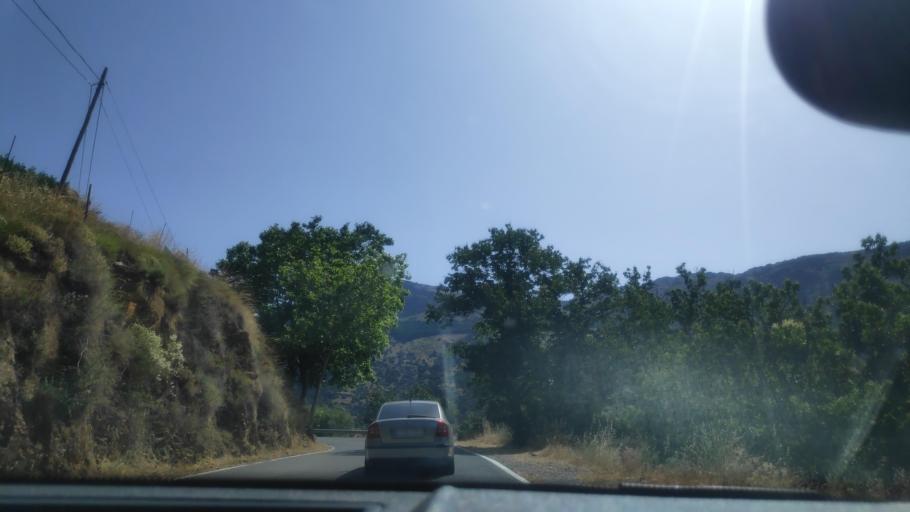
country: ES
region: Andalusia
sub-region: Provincia de Granada
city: Trevelez
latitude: 36.9891
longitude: -3.2713
